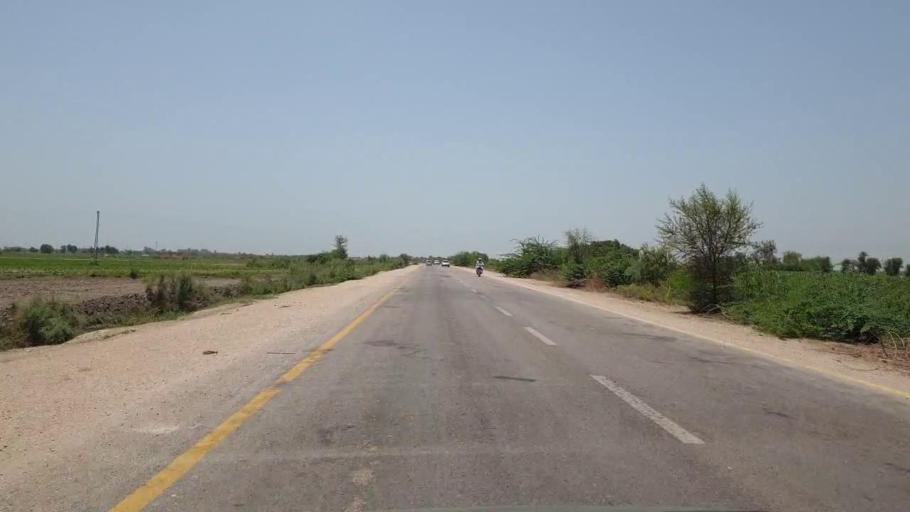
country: PK
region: Sindh
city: Sakrand
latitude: 26.1308
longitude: 68.3767
